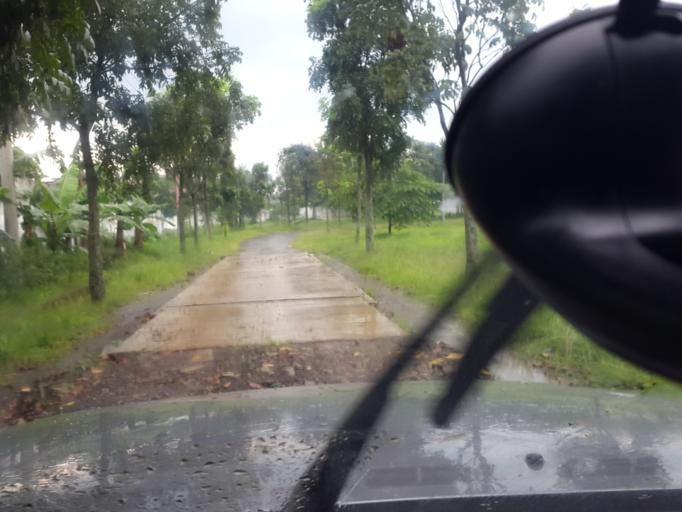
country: ID
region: West Java
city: Bandung
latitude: -6.9125
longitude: 107.6846
